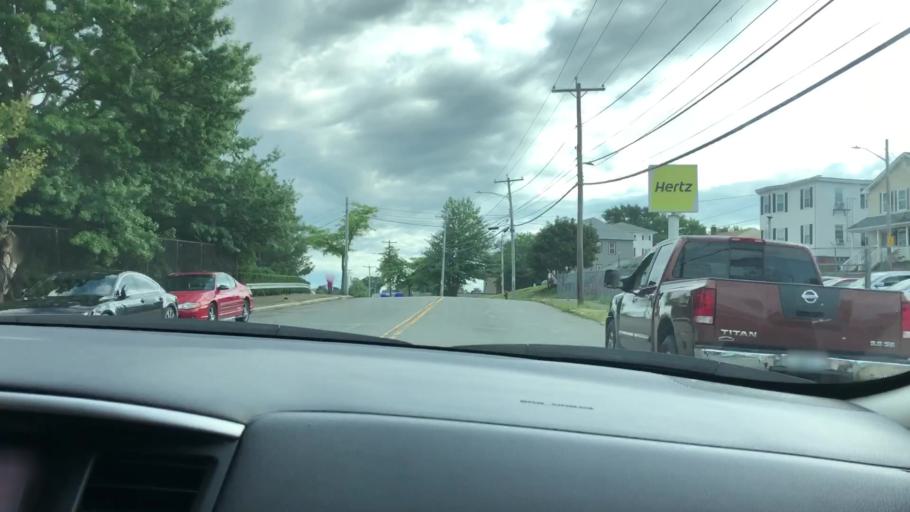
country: US
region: Rhode Island
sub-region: Providence County
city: Providence
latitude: 41.8543
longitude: -71.4122
